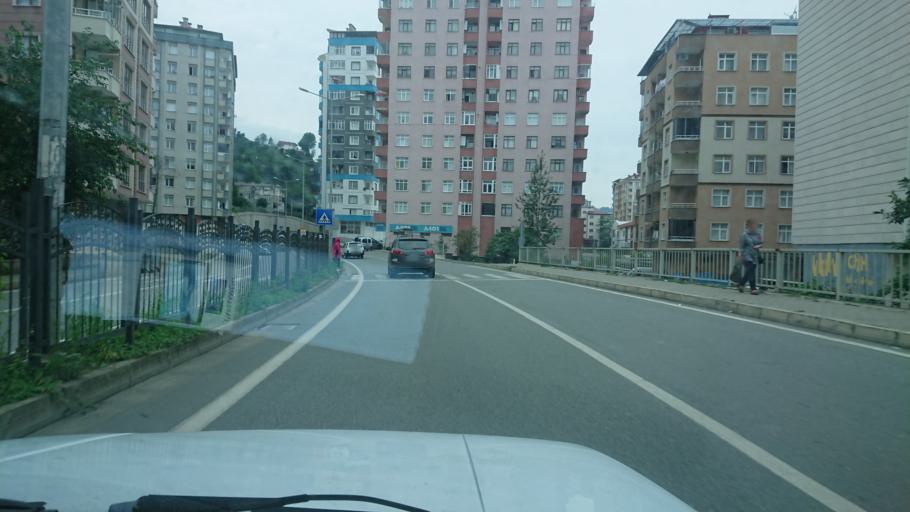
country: TR
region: Rize
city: Rize
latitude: 41.0222
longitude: 40.5347
